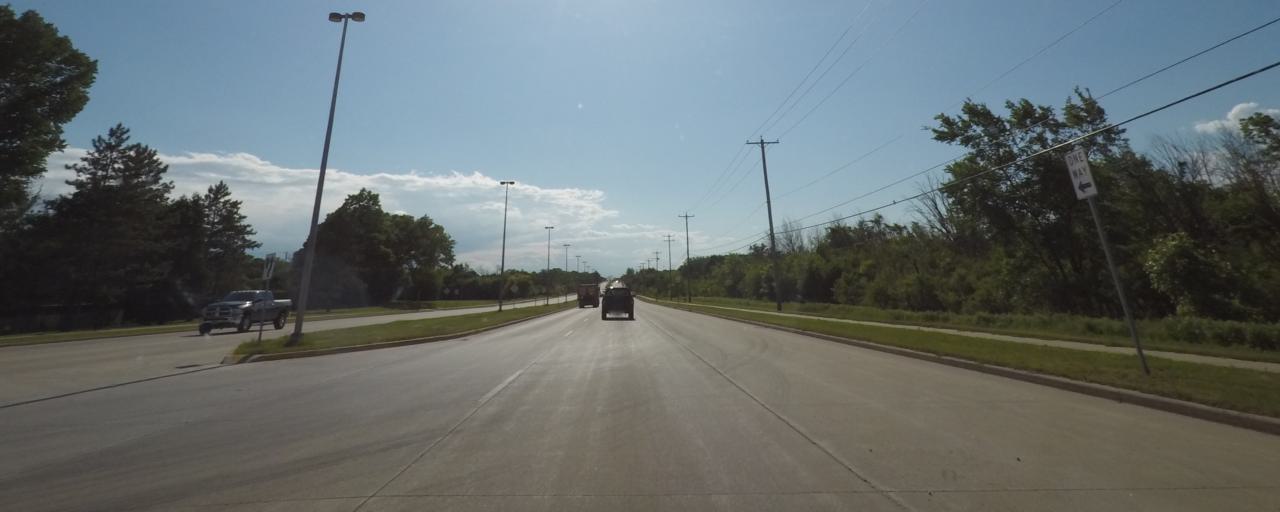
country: US
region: Wisconsin
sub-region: Milwaukee County
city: Greendale
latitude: 42.9160
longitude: -87.9932
